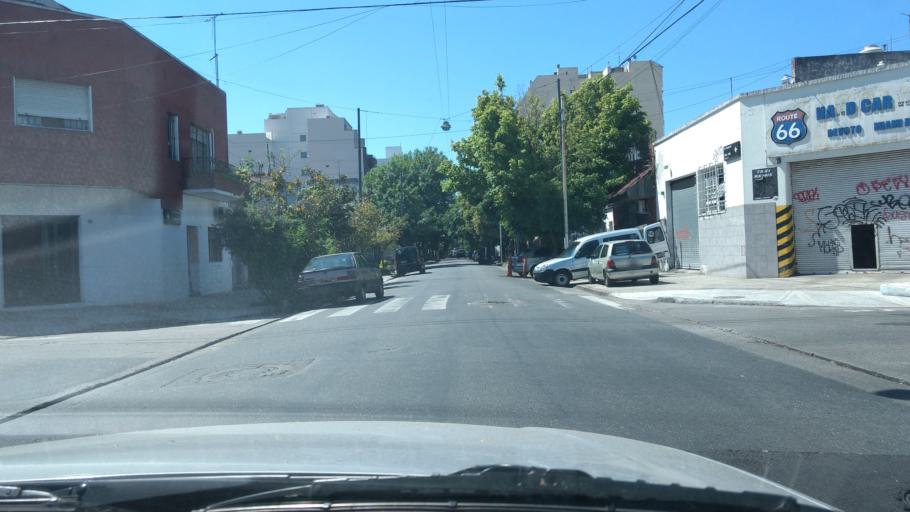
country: AR
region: Buenos Aires F.D.
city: Villa Santa Rita
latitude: -34.6140
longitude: -58.5063
